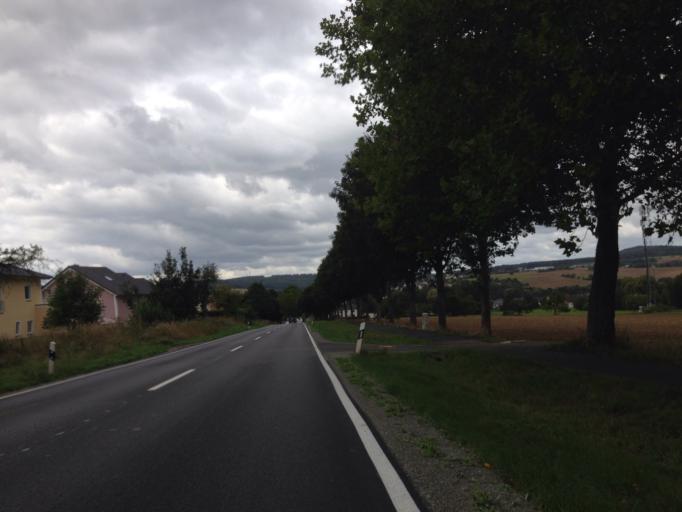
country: DE
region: Hesse
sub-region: Regierungsbezirk Giessen
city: Elz
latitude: 50.4153
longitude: 8.0529
